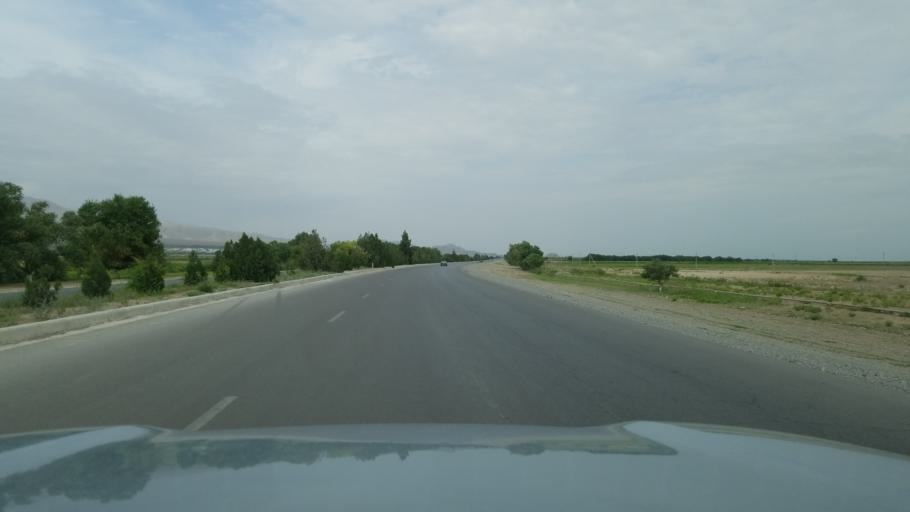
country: TM
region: Ahal
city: Arcabil
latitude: 38.1852
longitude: 57.8558
